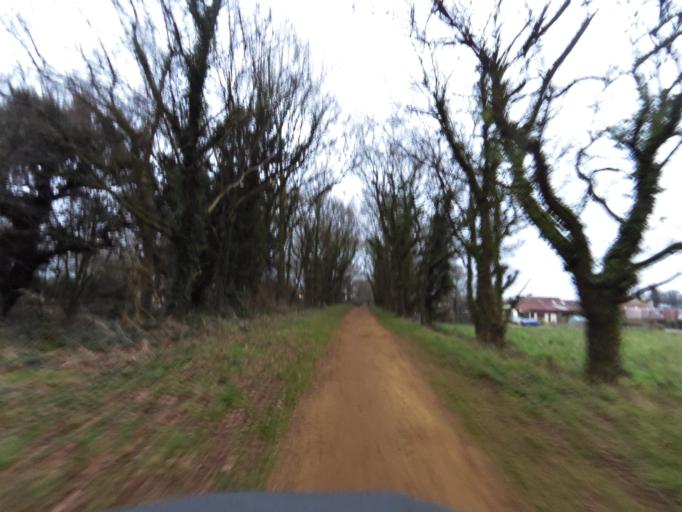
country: GB
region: England
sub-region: Norfolk
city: Horsford
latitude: 52.7032
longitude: 1.1947
